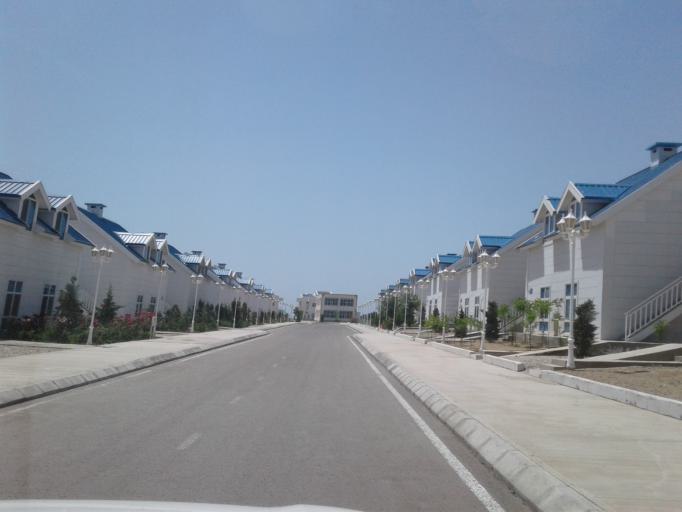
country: TM
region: Balkan
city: Turkmenbasy
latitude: 39.9875
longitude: 52.8281
